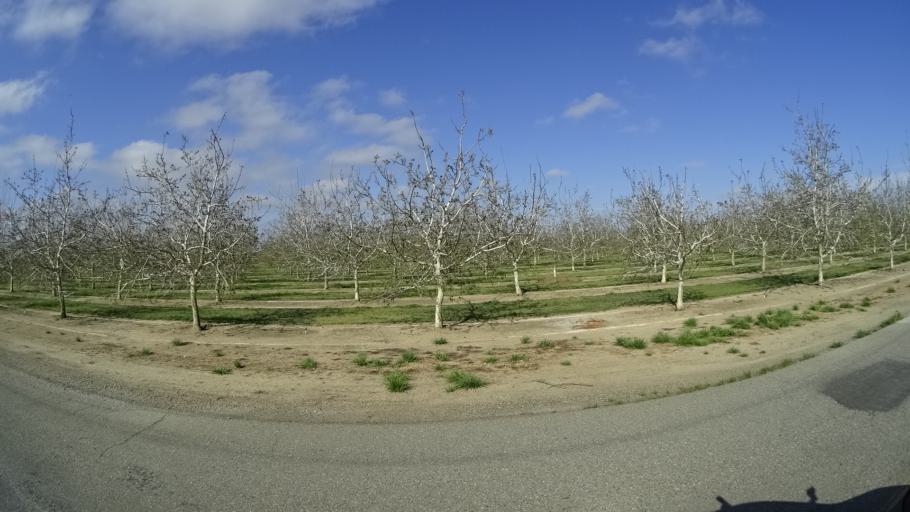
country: US
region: California
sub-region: Glenn County
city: Willows
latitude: 39.4885
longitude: -121.9677
